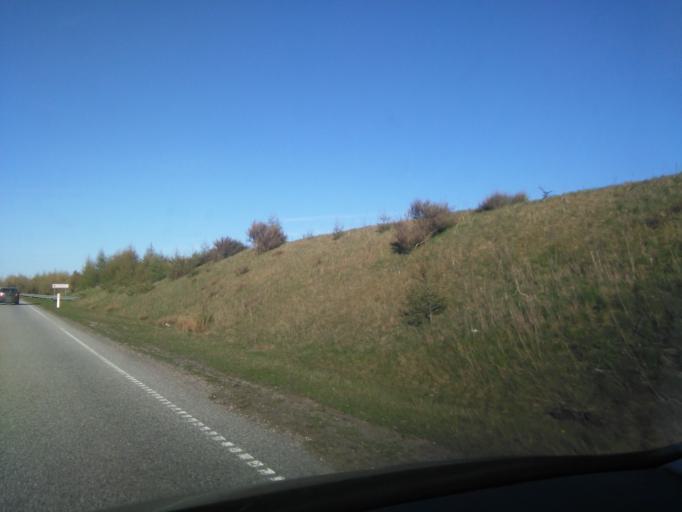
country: DK
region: Central Jutland
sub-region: Ringkobing-Skjern Kommune
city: Videbaek
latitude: 56.0945
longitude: 8.6016
